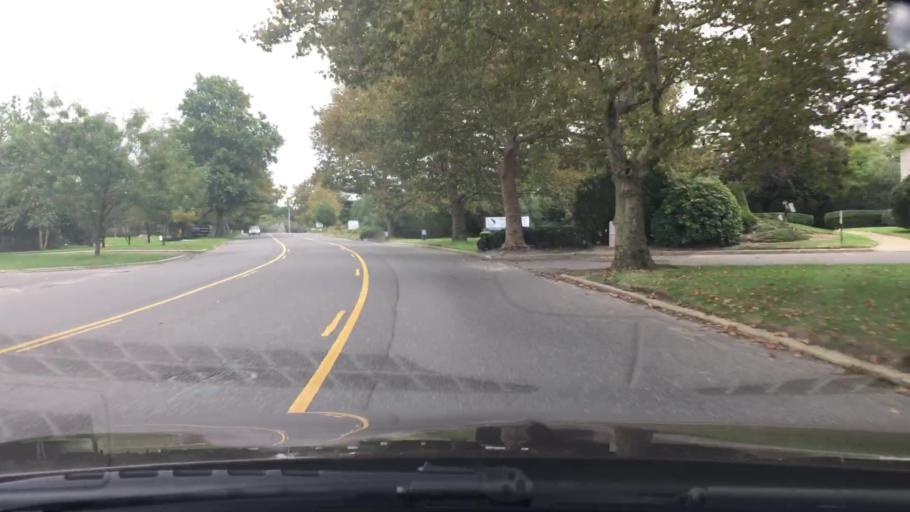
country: US
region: New York
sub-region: Suffolk County
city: Brentwood
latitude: 40.8168
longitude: -73.2532
